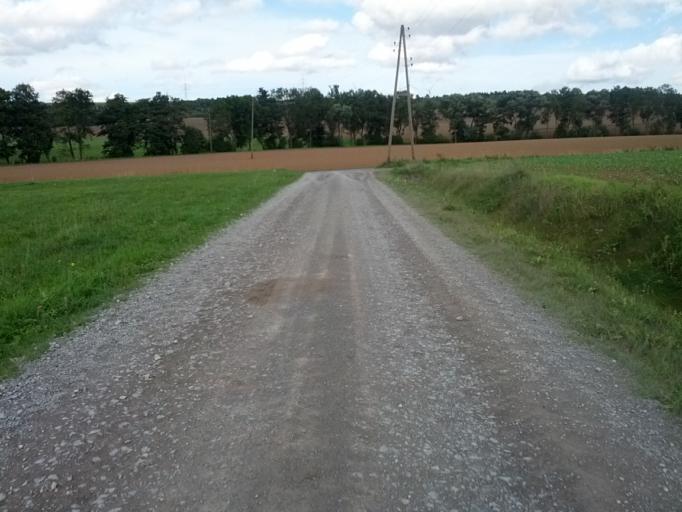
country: DE
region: Thuringia
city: Krauthausen
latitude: 51.0176
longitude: 10.2939
